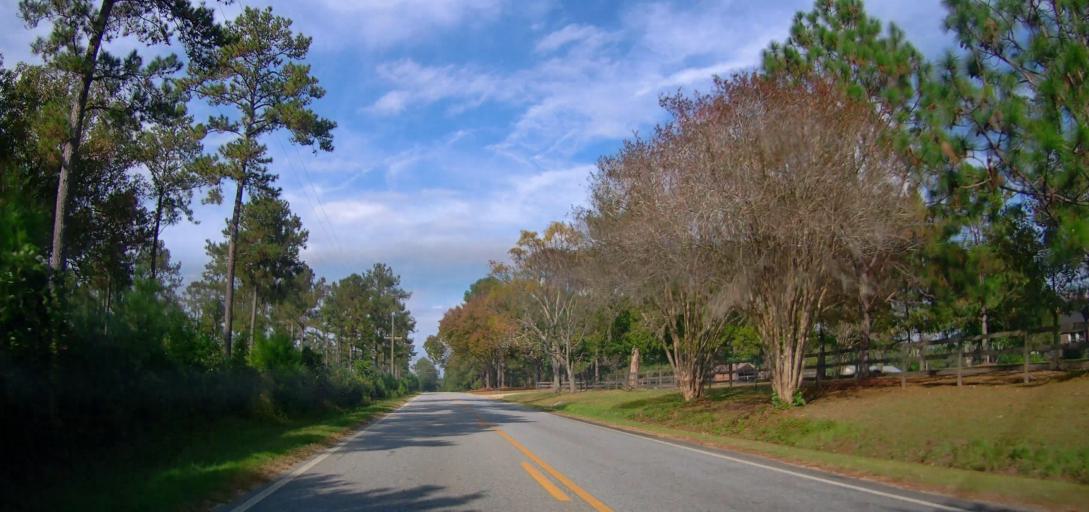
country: US
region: Georgia
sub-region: Thomas County
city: Thomasville
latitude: 30.8985
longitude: -84.0064
